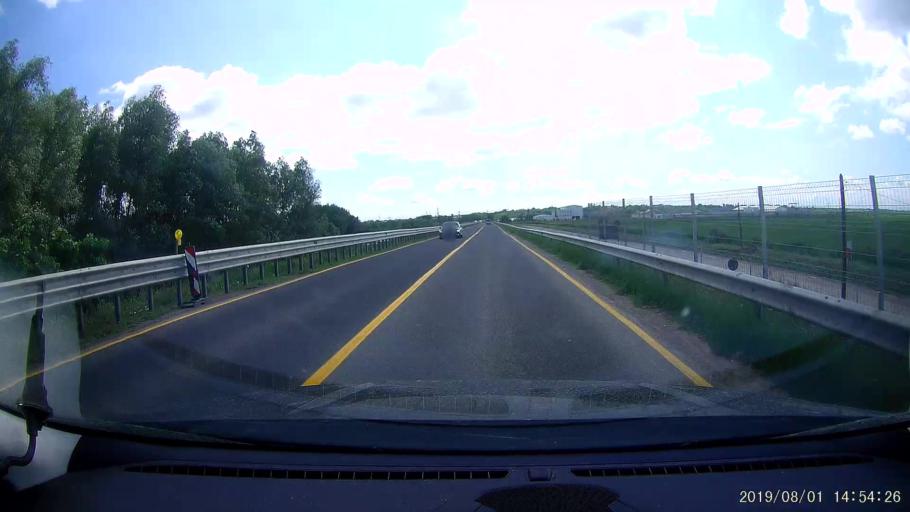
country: RO
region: Braila
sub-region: Municipiul Braila
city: Braila
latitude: 45.3184
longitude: 27.9890
